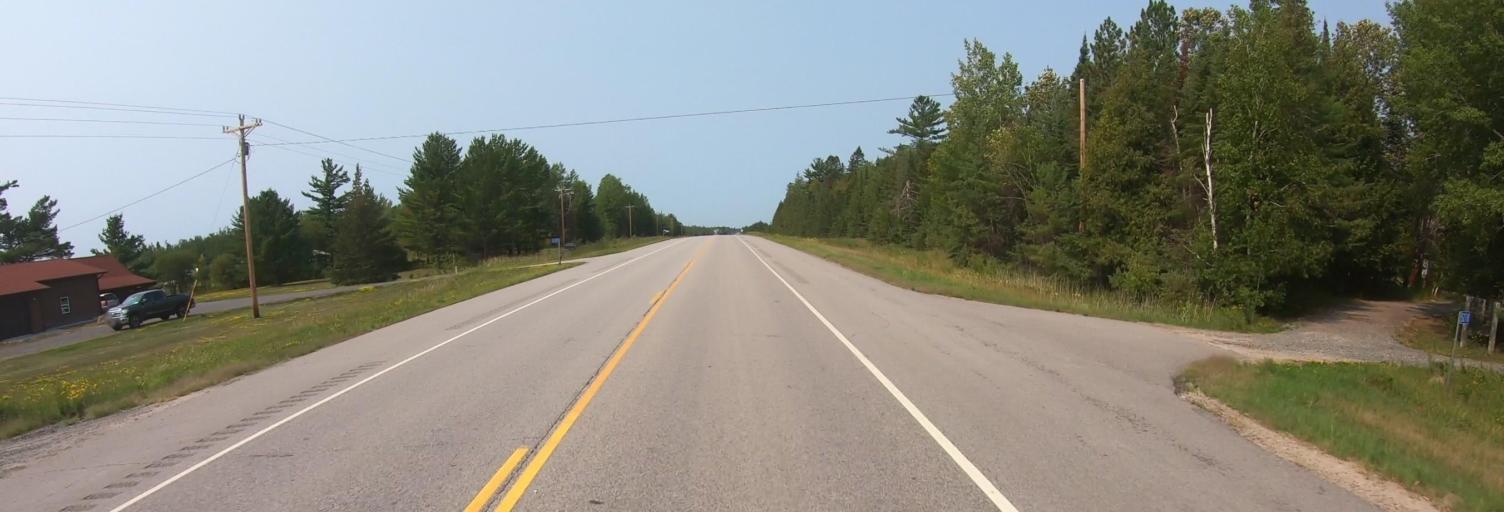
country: CA
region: Ontario
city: Fort Frances
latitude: 48.4103
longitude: -93.1680
